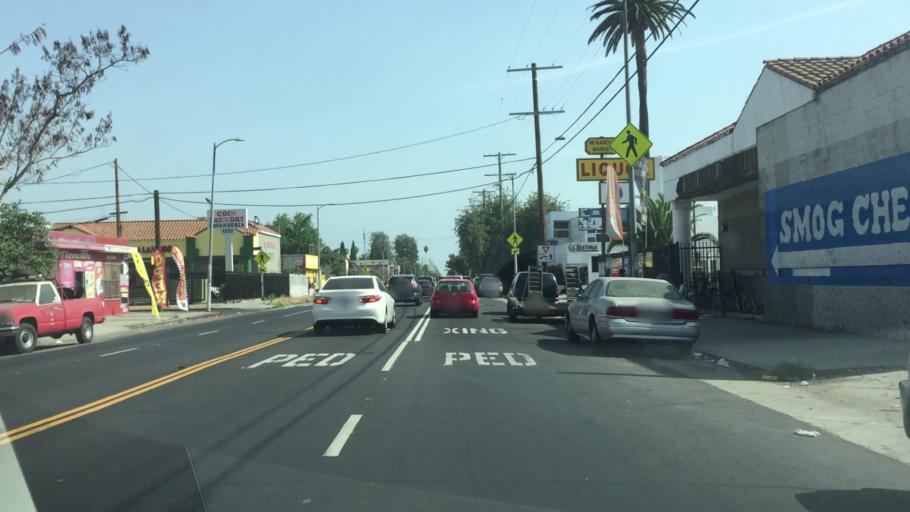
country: US
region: California
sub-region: Los Angeles County
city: Huntington Park
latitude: 33.9989
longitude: -118.2478
